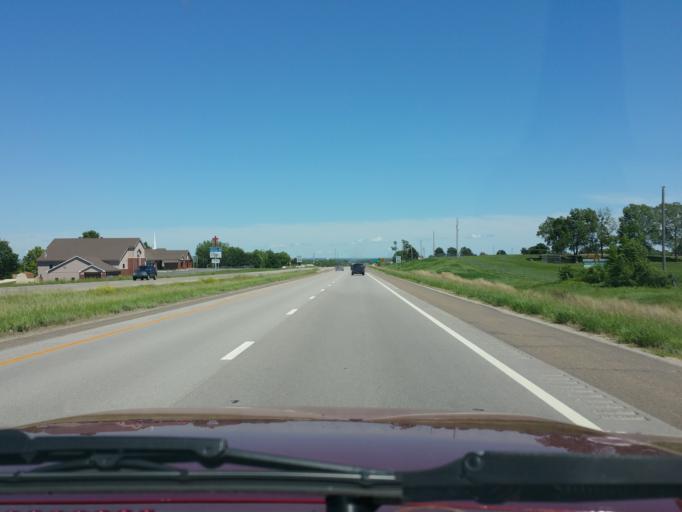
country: US
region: Kansas
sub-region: Pottawatomie County
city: Wamego
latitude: 39.2103
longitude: -96.3302
